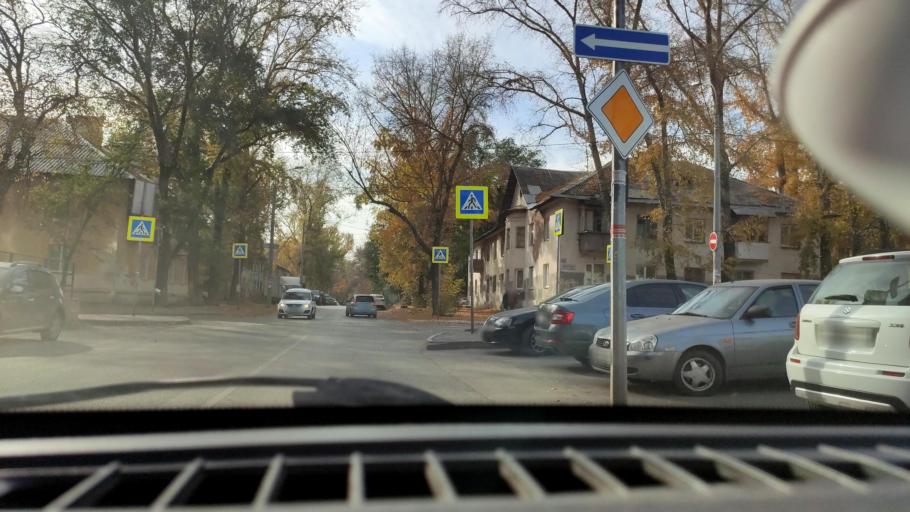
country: RU
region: Samara
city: Samara
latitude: 53.2293
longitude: 50.2612
